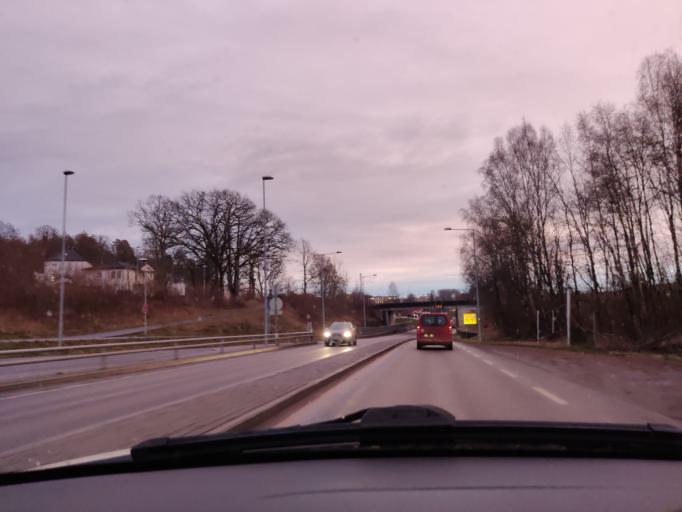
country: NO
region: Vestfold
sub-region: Tonsberg
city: Tonsberg
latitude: 59.2832
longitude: 10.3976
